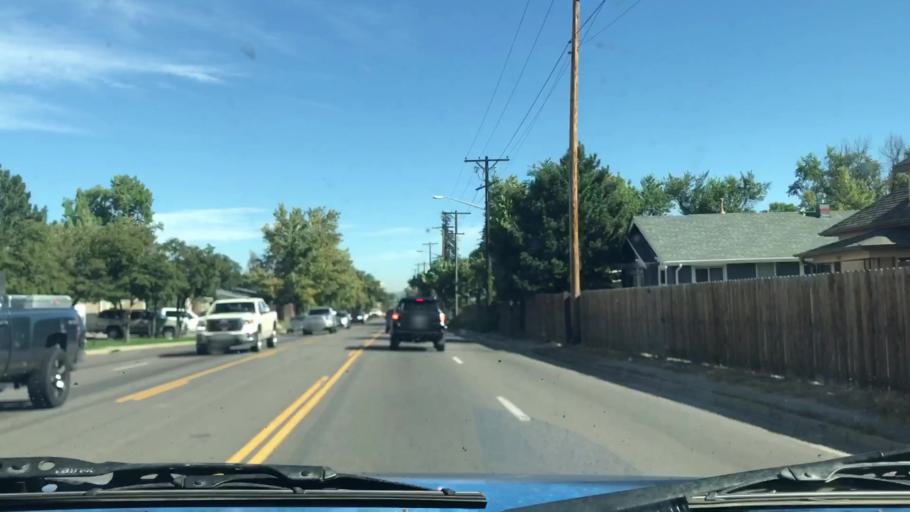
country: US
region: Colorado
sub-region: Jefferson County
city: Edgewater
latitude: 39.7701
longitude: -105.0532
